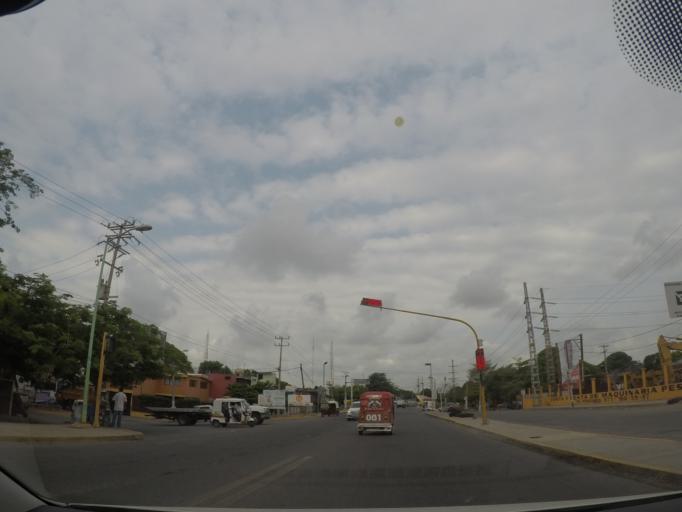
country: MX
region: Oaxaca
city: Juchitan de Zaragoza
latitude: 16.4473
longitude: -95.0168
